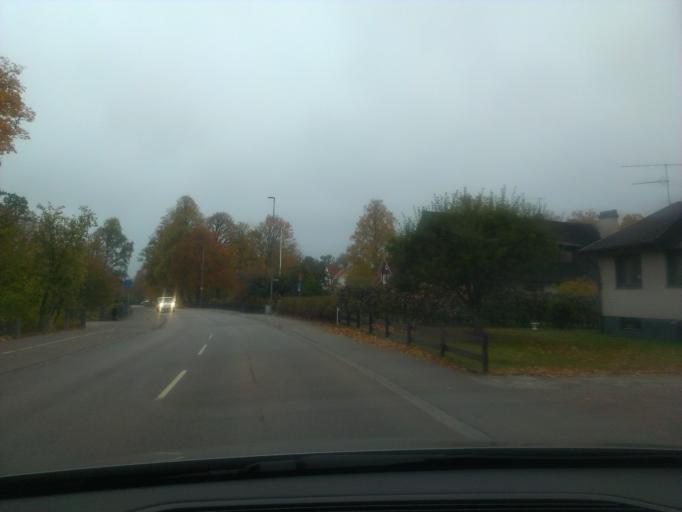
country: SE
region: Kronoberg
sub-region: Vaxjo Kommun
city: Vaexjoe
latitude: 56.9050
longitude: 14.7387
